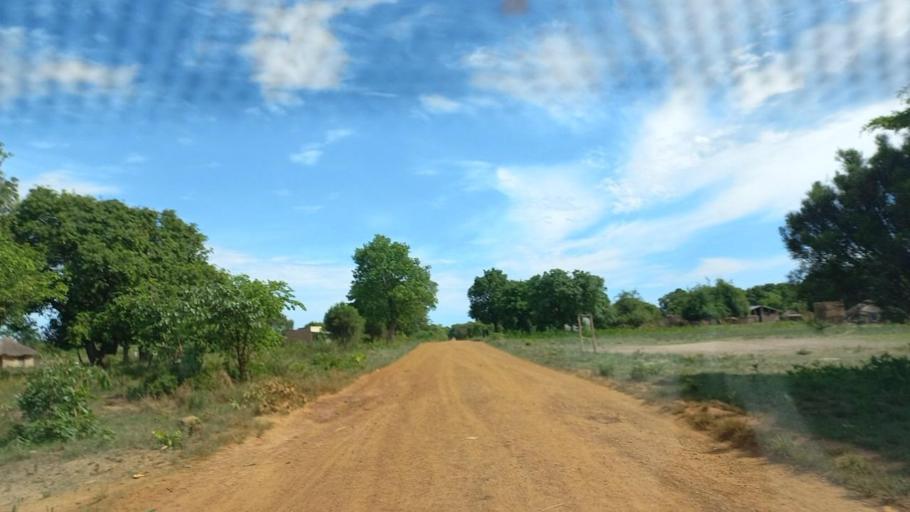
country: ZM
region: North-Western
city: Kabompo
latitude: -13.0611
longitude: 24.2192
